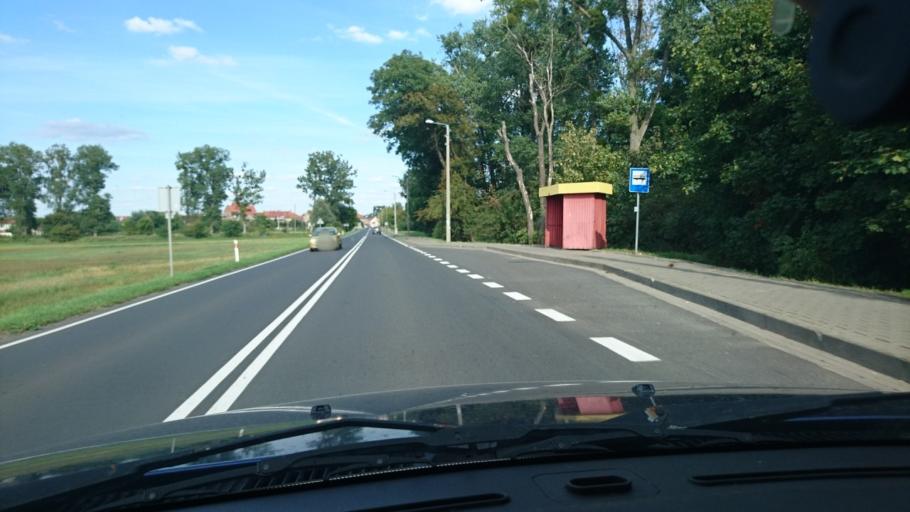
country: PL
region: Greater Poland Voivodeship
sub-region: Powiat krotoszynski
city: Kobylin
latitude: 51.7112
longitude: 17.2194
